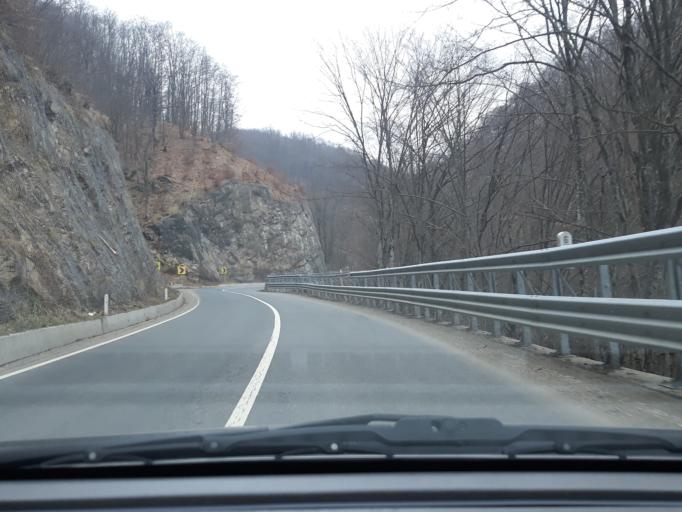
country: RO
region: Bihor
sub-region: Oras Alesd
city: Pestis
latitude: 47.1170
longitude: 22.4098
